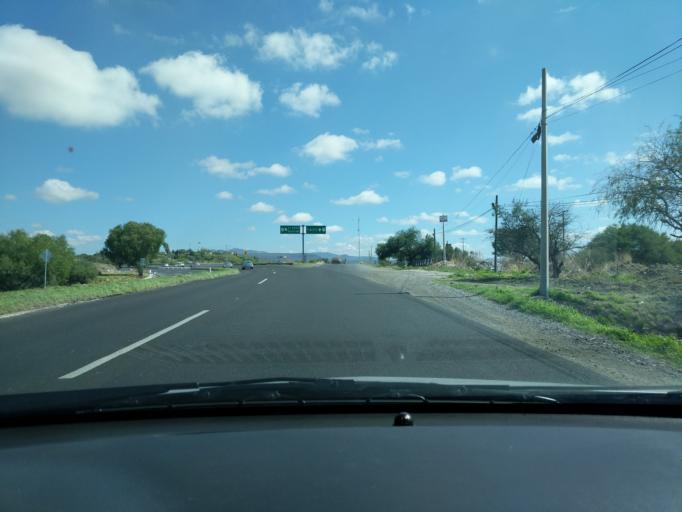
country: MX
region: Queretaro
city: Tlacote el Bajo
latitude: 20.6487
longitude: -100.5018
